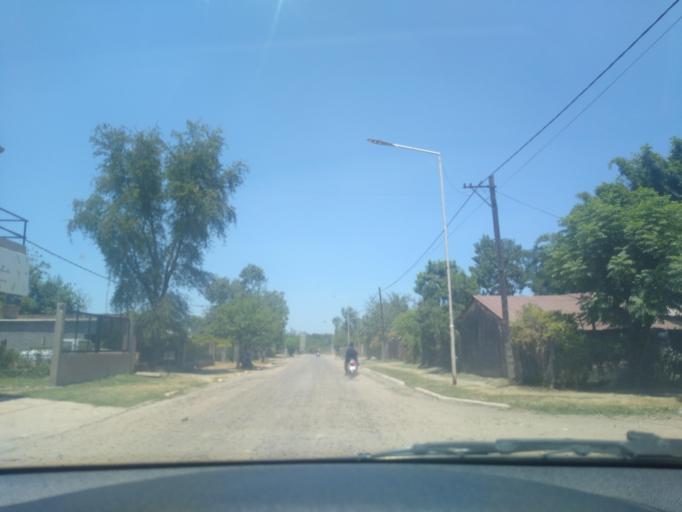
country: AR
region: Chaco
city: Puerto Tirol
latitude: -27.3840
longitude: -59.0882
